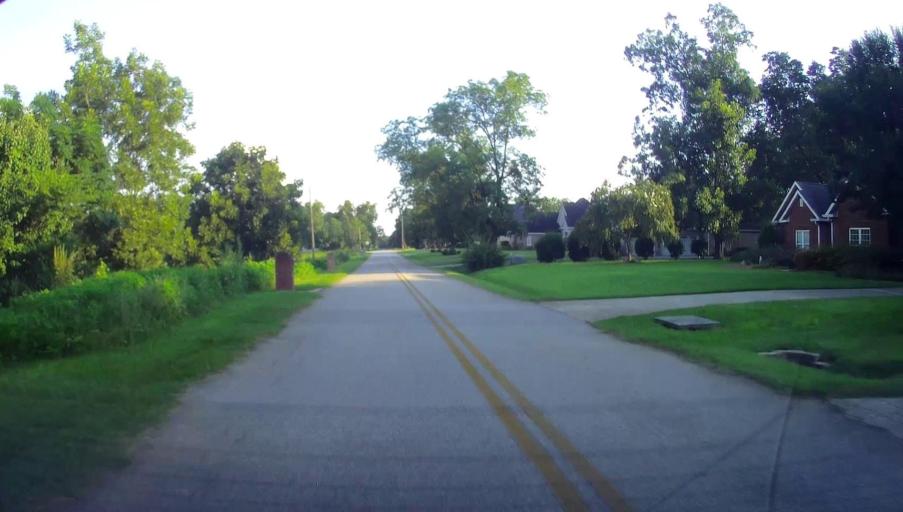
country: US
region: Georgia
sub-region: Peach County
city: Byron
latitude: 32.6462
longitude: -83.7916
